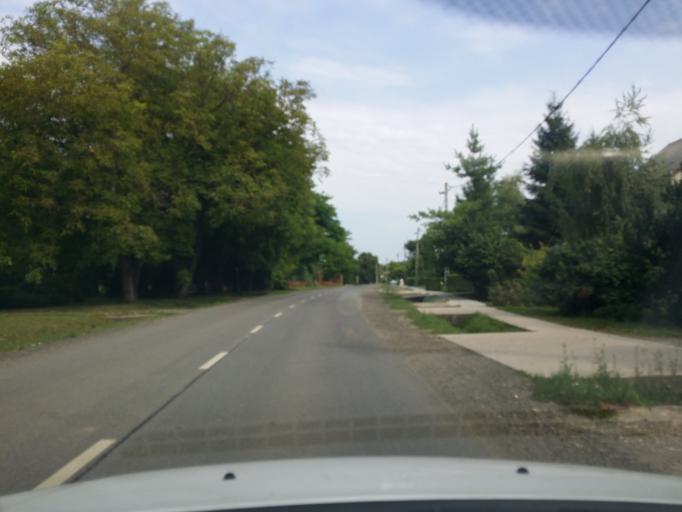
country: HU
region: Pest
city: Acsa
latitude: 47.7813
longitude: 19.3627
